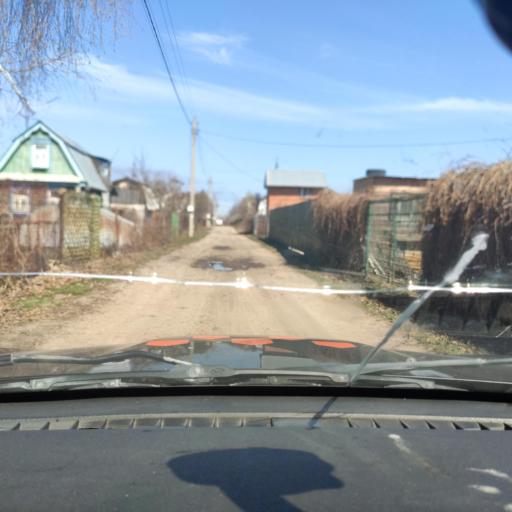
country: RU
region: Samara
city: Tol'yatti
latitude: 53.5855
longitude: 49.3138
